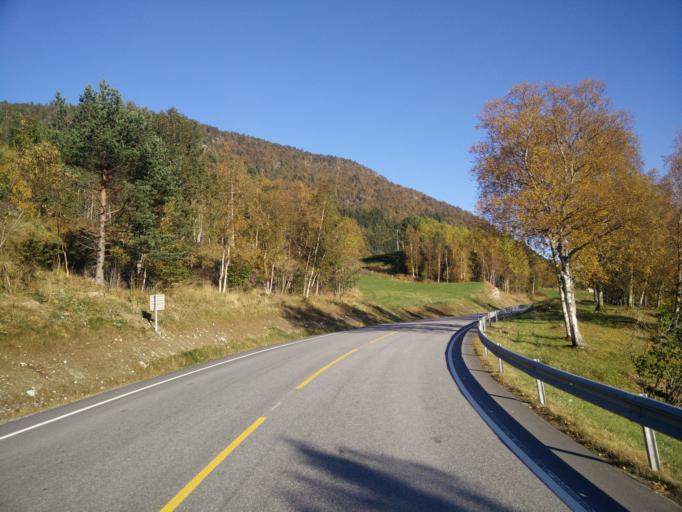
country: NO
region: More og Romsdal
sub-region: Tingvoll
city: Tingvoll
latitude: 63.0491
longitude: 8.0828
